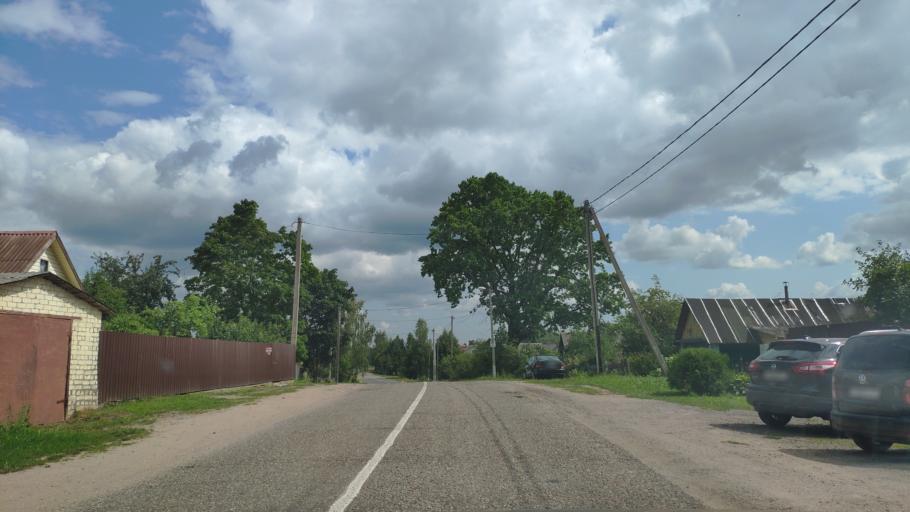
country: BY
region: Minsk
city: Khatsyezhyna
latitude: 53.8829
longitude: 27.2738
